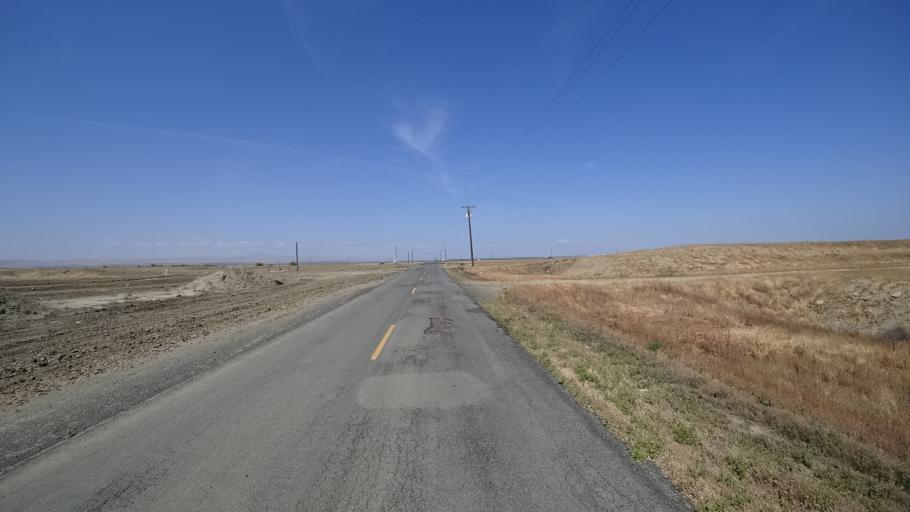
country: US
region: California
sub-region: Kings County
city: Kettleman City
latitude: 36.0941
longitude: -119.9215
